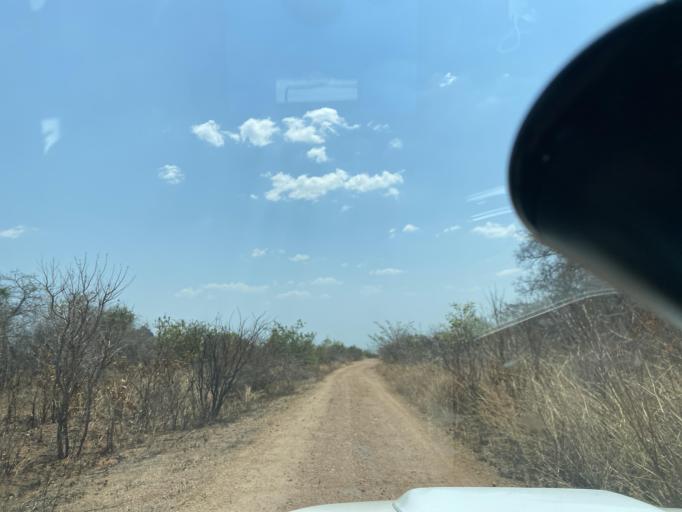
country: ZM
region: Lusaka
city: Lusaka
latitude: -15.5063
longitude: 27.9732
